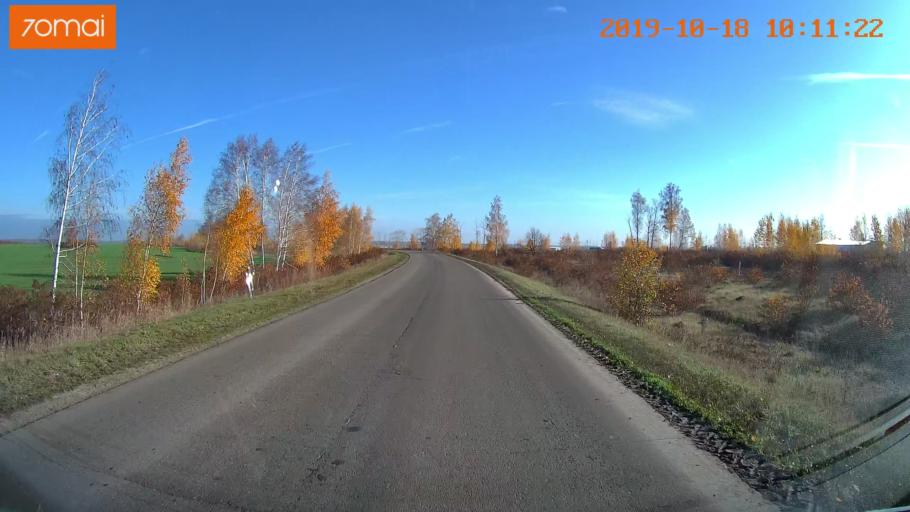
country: RU
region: Tula
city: Kurkino
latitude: 53.3817
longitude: 38.4970
